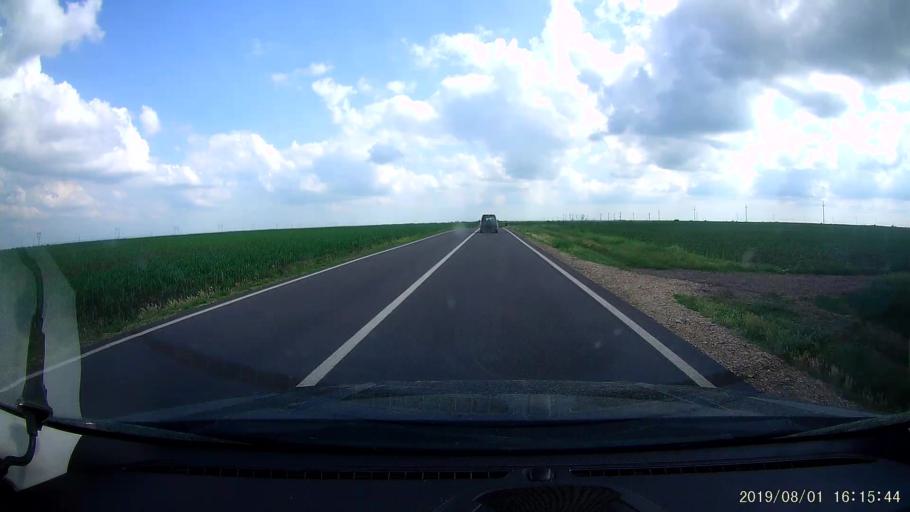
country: RO
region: Calarasi
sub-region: Comuna Stefan Voda
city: Stefan Voda
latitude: 44.3326
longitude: 27.3601
